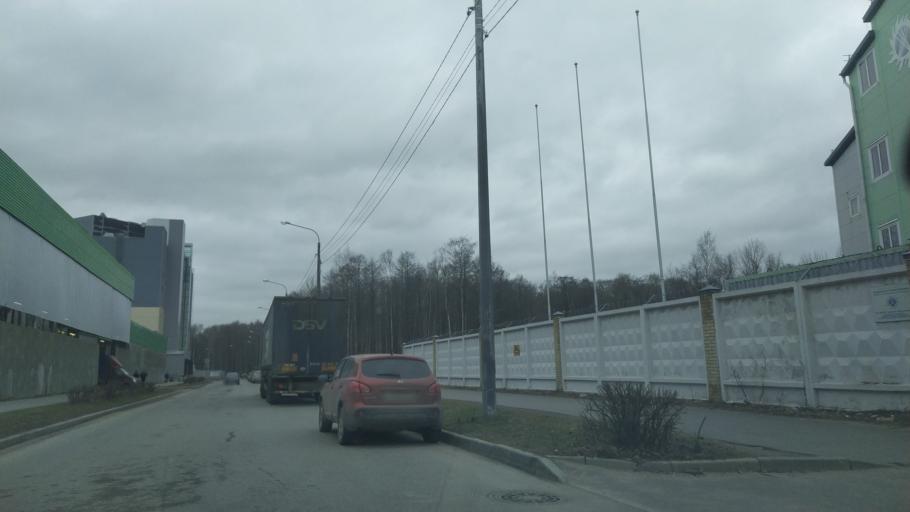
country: RU
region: Leningrad
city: Chernaya Rechka
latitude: 60.0035
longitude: 30.3027
